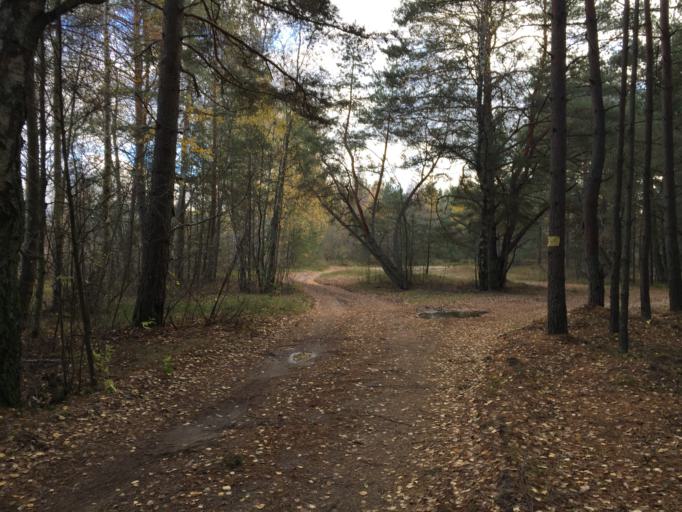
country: LV
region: Carnikava
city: Carnikava
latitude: 57.1509
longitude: 24.2602
